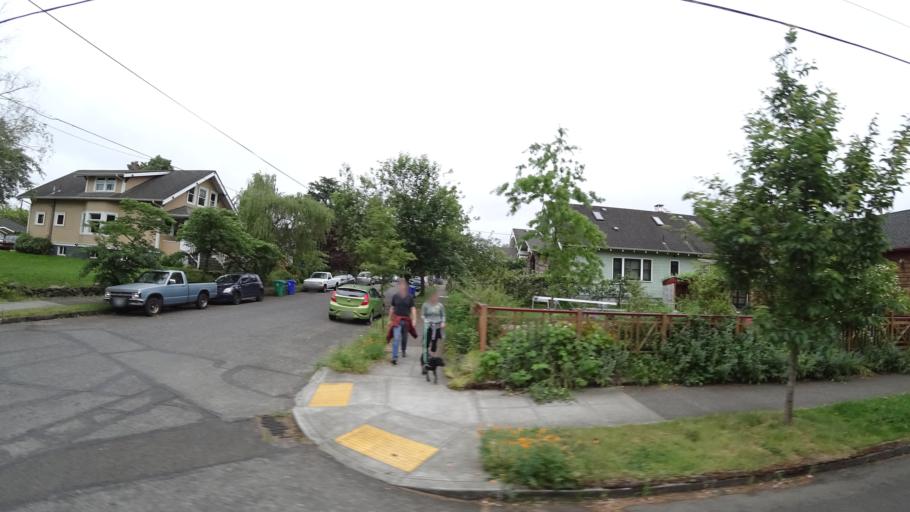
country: US
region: Oregon
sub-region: Multnomah County
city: Portland
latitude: 45.5563
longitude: -122.6370
